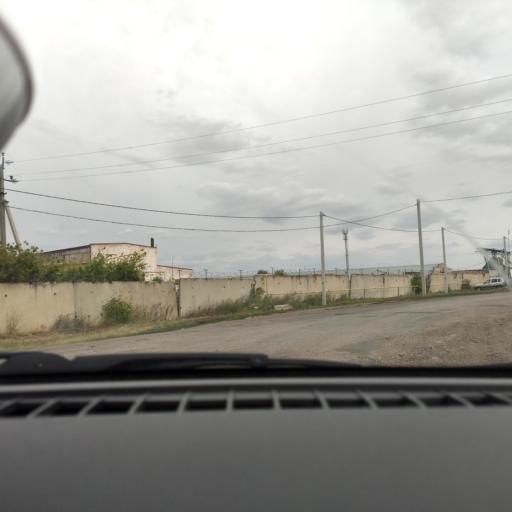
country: RU
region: Samara
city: Georgiyevka
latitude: 53.4721
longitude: 50.9412
